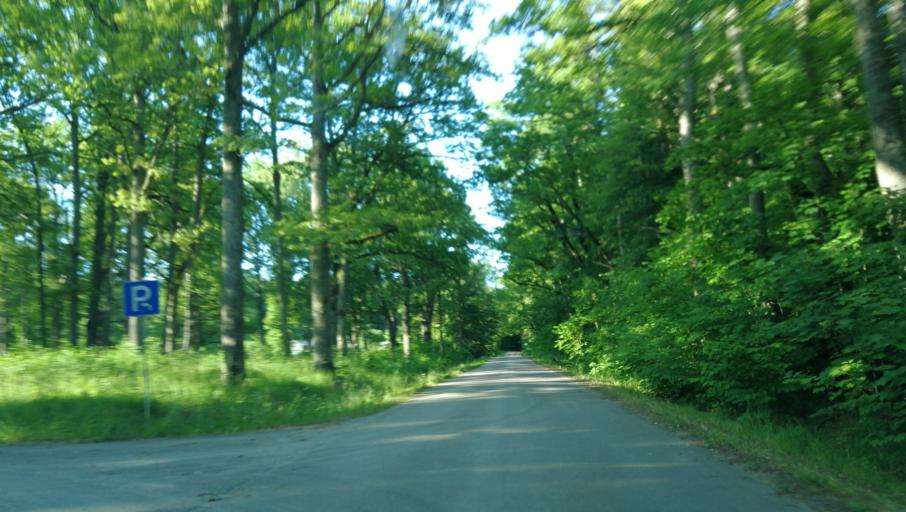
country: LV
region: Pargaujas
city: Stalbe
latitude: 57.3617
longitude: 25.0925
